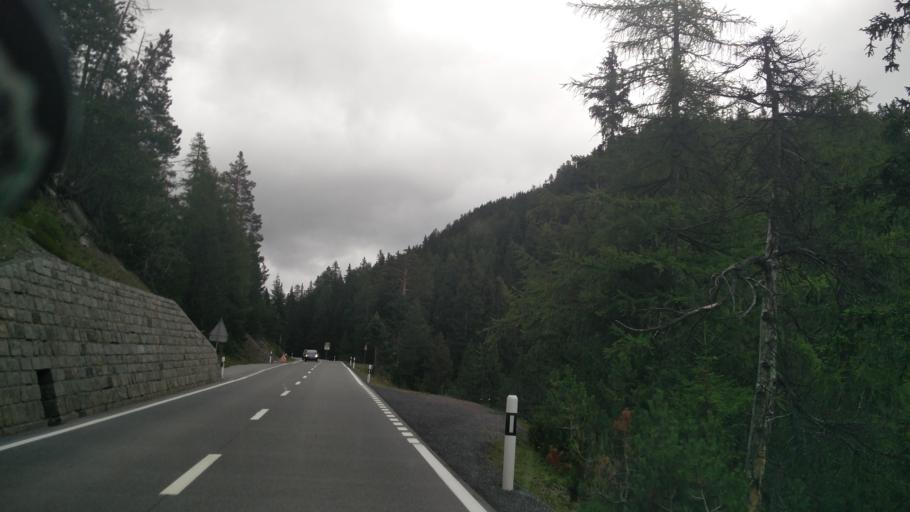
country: CH
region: Grisons
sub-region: Inn District
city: Zernez
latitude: 46.6853
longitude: 10.1487
